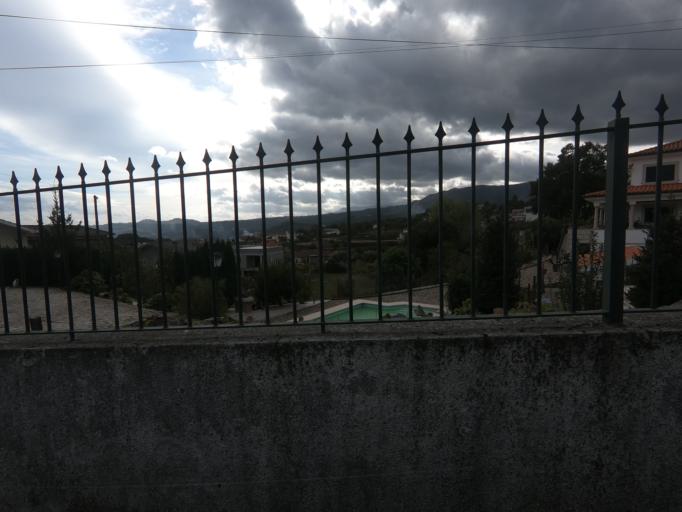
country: PT
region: Vila Real
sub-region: Vila Real
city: Vila Real
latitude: 41.3214
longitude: -7.7684
